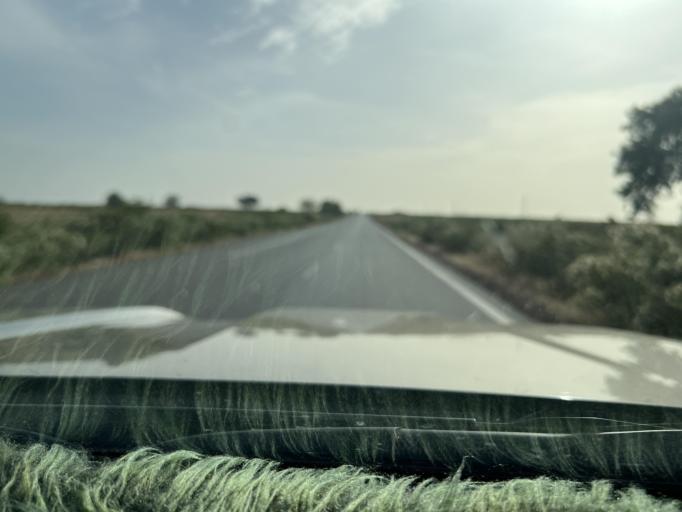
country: ML
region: Segou
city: Baroueli
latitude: 12.9564
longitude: -6.7268
